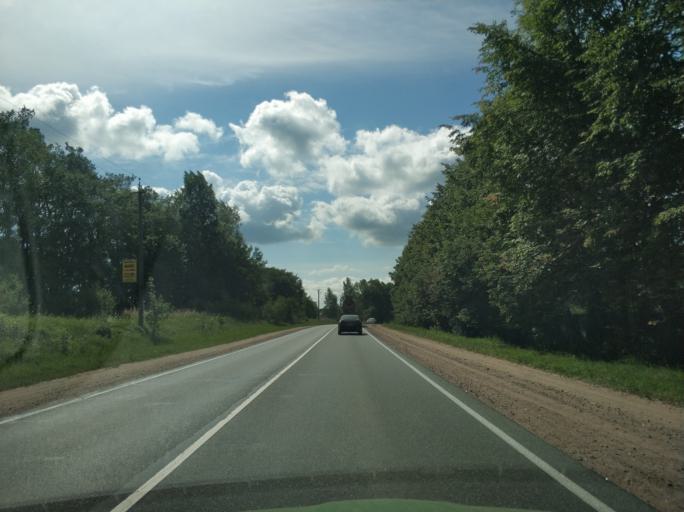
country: RU
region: Leningrad
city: Romanovka
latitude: 60.0576
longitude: 30.7417
